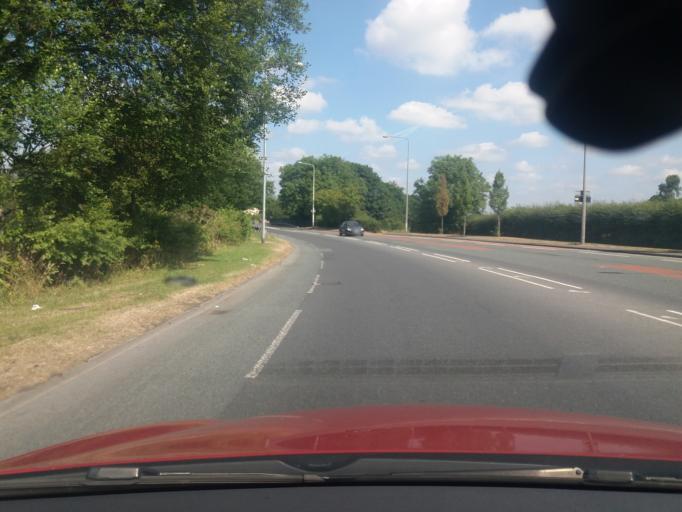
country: GB
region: England
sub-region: Lancashire
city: Adlington
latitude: 53.6291
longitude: -2.6100
